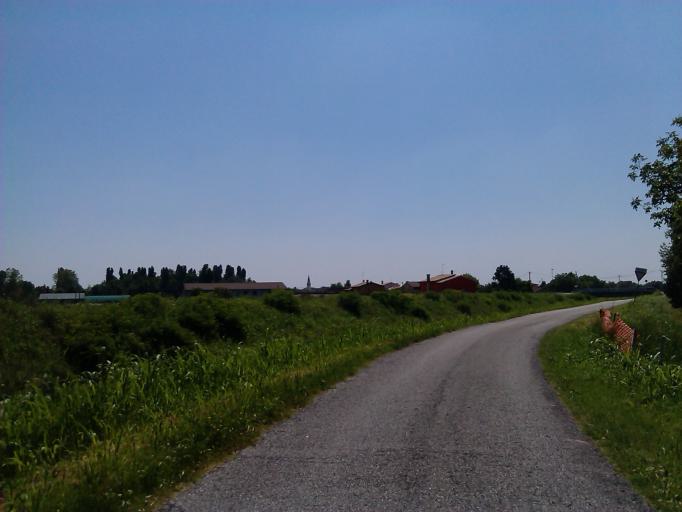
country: IT
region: Veneto
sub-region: Provincia di Padova
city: Loreggia
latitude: 45.6019
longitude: 11.9330
